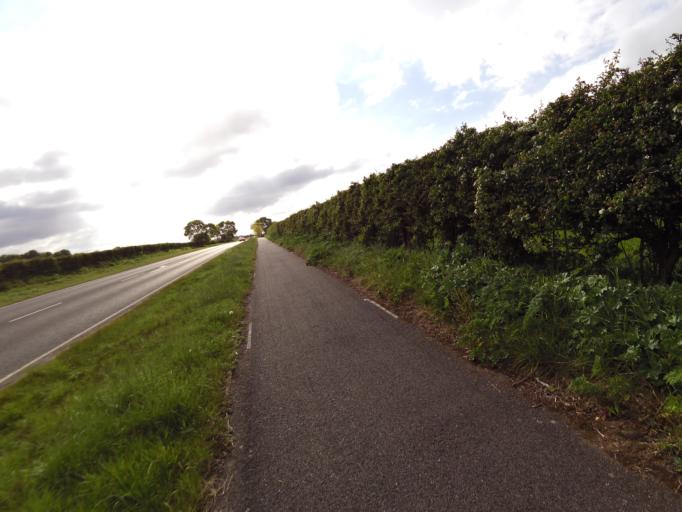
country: GB
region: England
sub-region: Cambridgeshire
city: Bottisham
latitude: 52.2192
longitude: 0.2437
